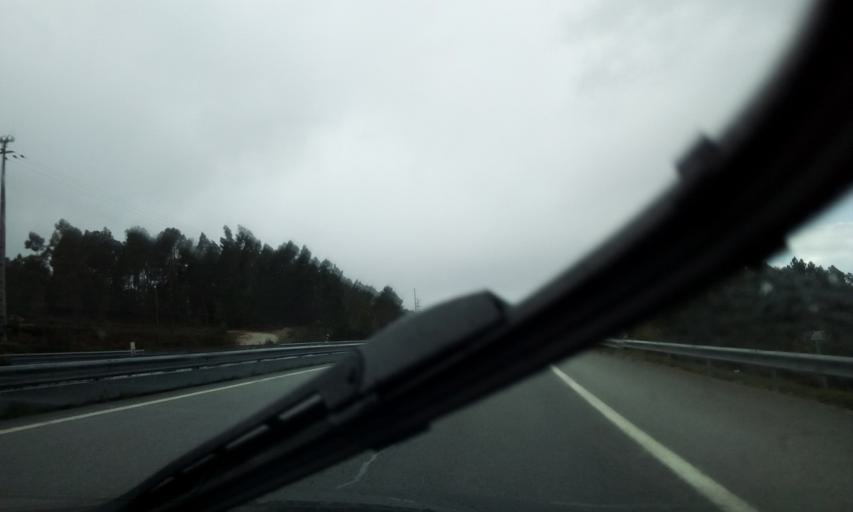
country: PT
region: Viseu
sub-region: Mangualde
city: Mangualde
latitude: 40.6133
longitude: -7.6706
